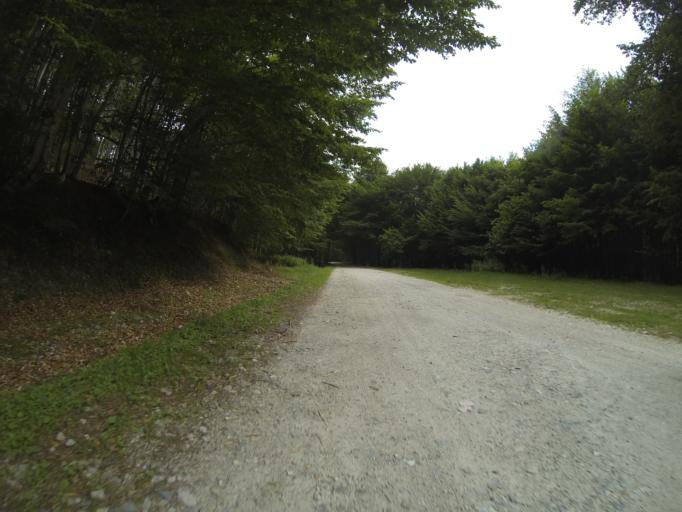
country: RO
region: Gorj
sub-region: Comuna Polovragi
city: Polovragi
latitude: 45.2251
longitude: 23.7715
